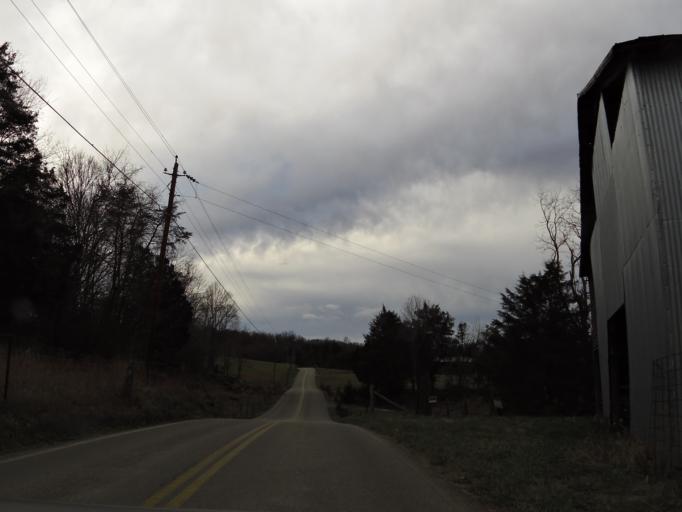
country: US
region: Tennessee
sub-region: Greene County
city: Tusculum
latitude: 36.2069
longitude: -82.7455
